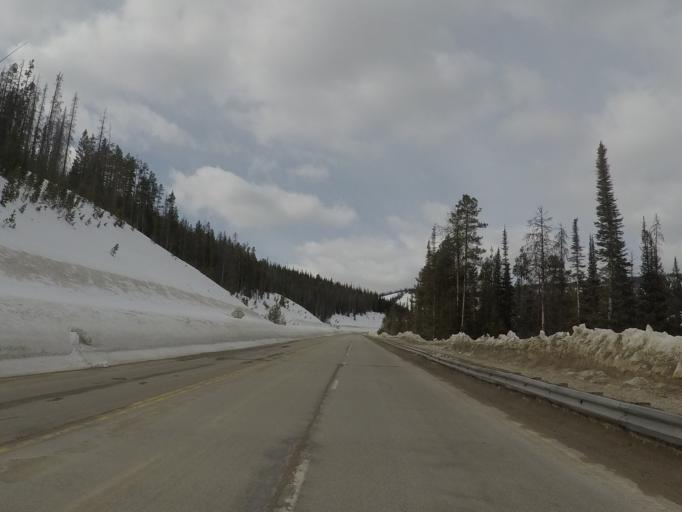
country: US
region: Idaho
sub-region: Lemhi County
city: Salmon
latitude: 45.7037
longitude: -113.9382
